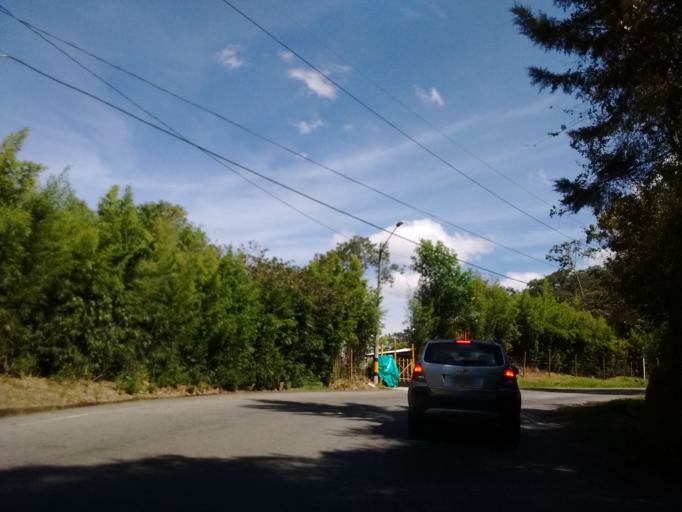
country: CO
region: Antioquia
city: Medellin
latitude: 6.2297
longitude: -75.5156
